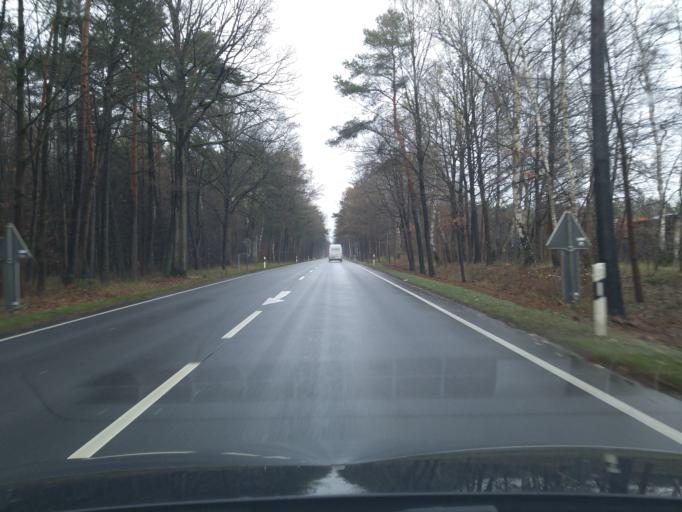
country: DE
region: Lower Saxony
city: Dedelstorf
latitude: 52.6885
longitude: 10.4732
